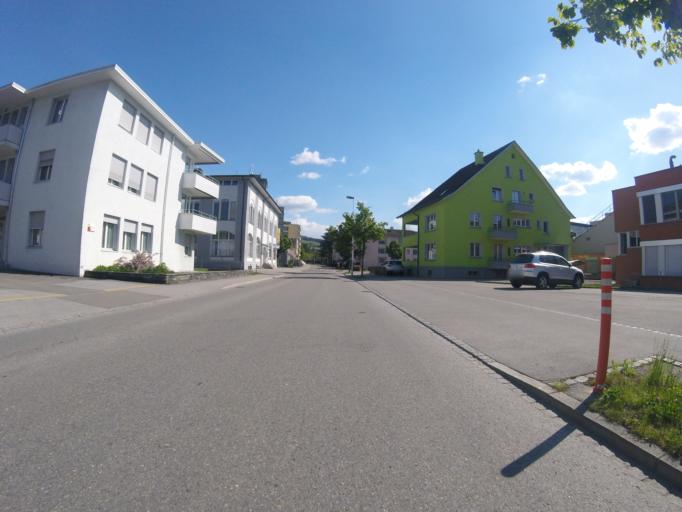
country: CH
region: Saint Gallen
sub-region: Wahlkreis St. Gallen
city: Gossau
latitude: 47.4140
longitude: 9.2548
